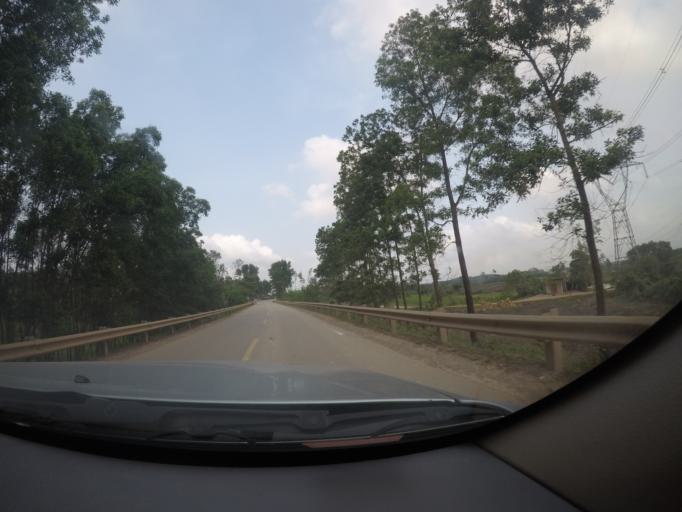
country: VN
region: Quang Binh
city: Kien Giang
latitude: 17.1174
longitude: 106.8116
